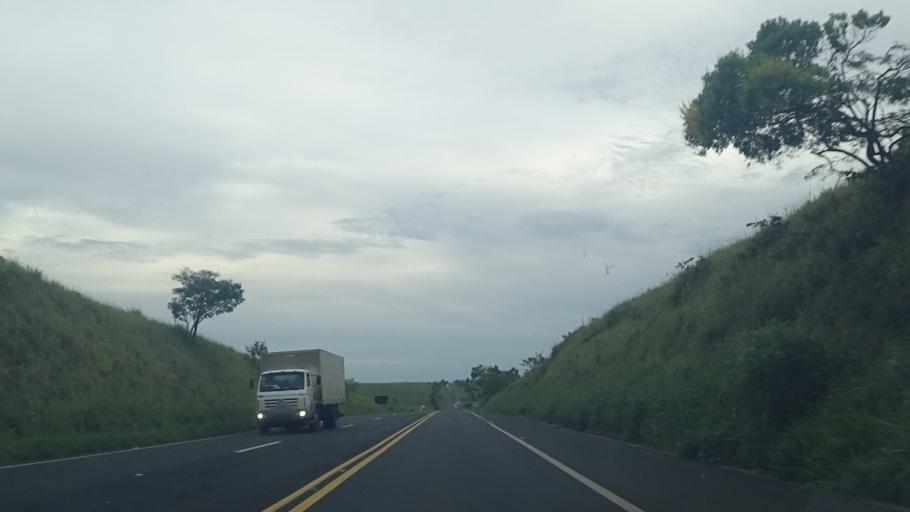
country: BR
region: Sao Paulo
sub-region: Martinopolis
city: Martinopolis
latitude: -22.0788
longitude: -51.1165
